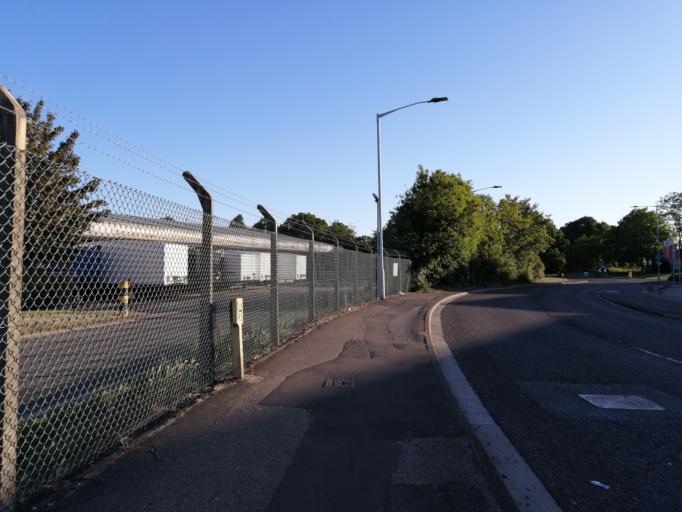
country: GB
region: England
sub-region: Peterborough
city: Peterborough
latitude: 52.5916
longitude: -0.2650
